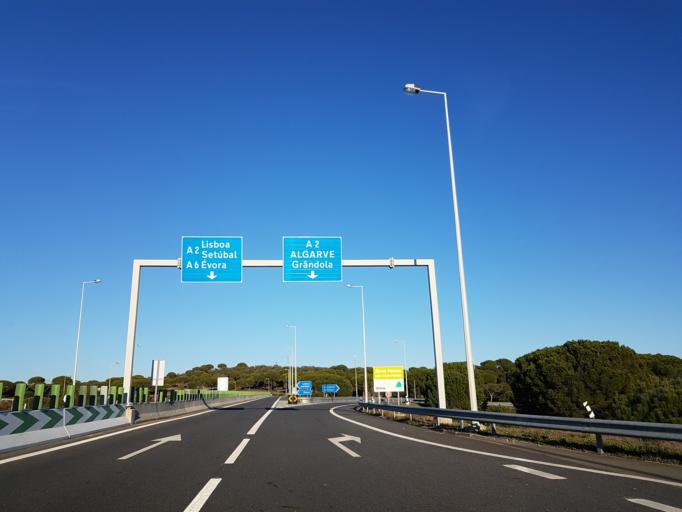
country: PT
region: Setubal
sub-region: Alcacer do Sal
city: Alcacer do Sal
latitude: 38.4167
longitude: -8.5133
